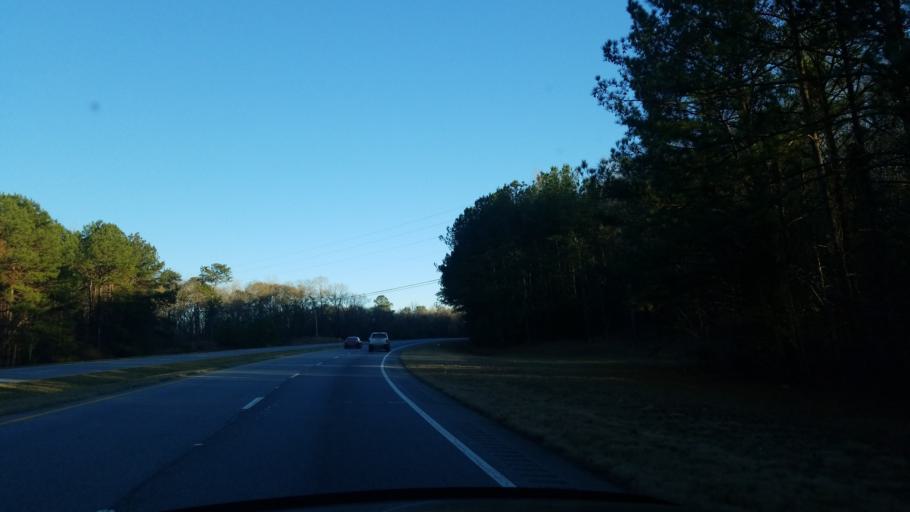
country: US
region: Georgia
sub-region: Chattahoochee County
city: Cusseta
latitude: 32.2709
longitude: -84.7465
